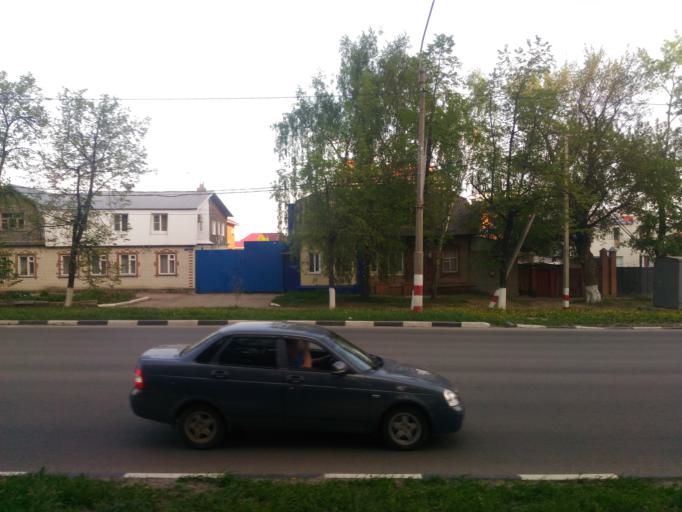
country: RU
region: Ulyanovsk
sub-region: Ulyanovskiy Rayon
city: Ulyanovsk
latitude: 54.3022
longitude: 48.3846
